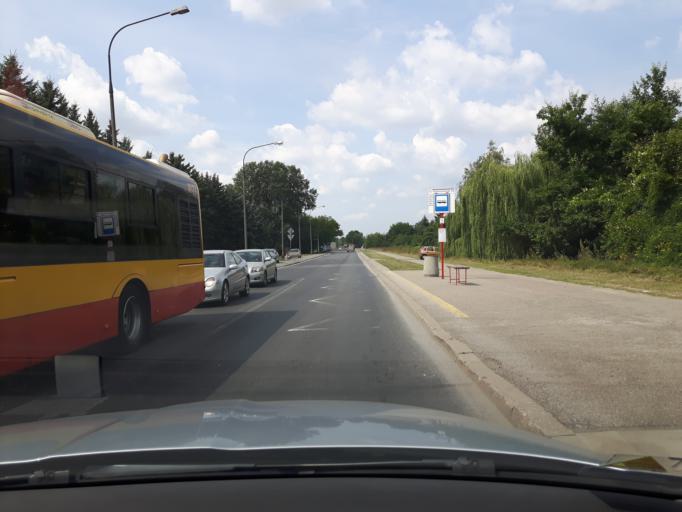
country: PL
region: Masovian Voivodeship
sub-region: Warszawa
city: Wilanow
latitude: 52.1905
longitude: 21.0829
